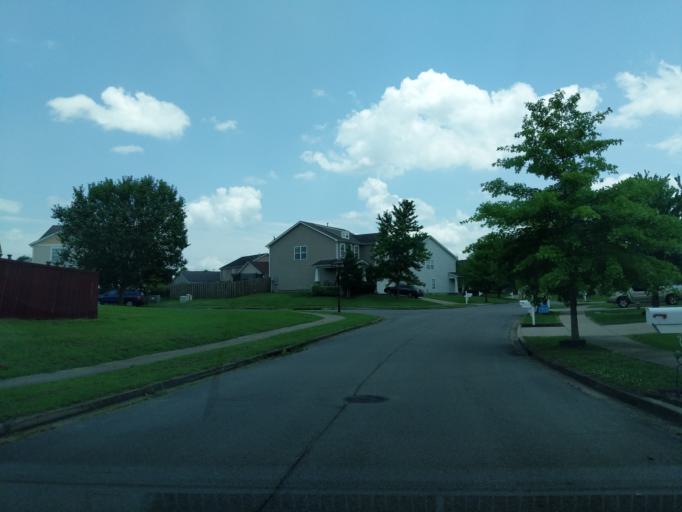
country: US
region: Tennessee
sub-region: Davidson County
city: Goodlettsville
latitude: 36.3003
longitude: -86.7277
